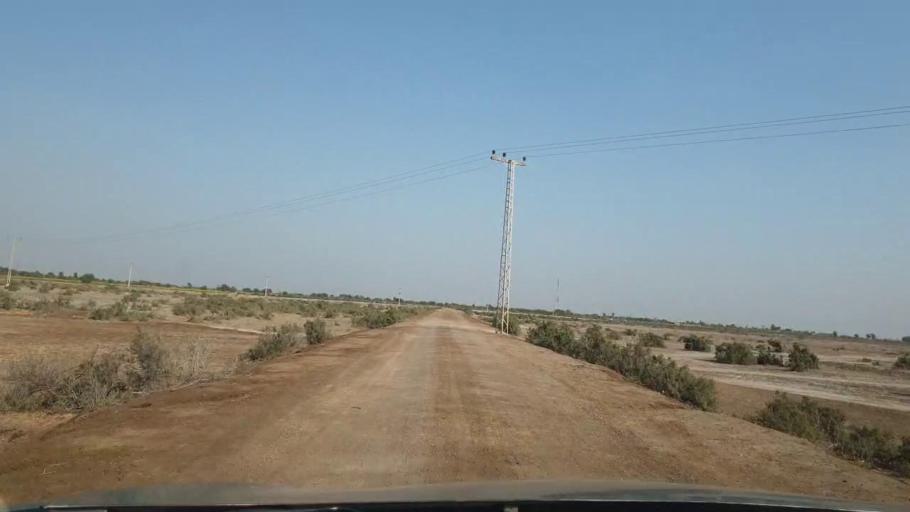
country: PK
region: Sindh
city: Berani
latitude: 25.6223
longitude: 68.8399
